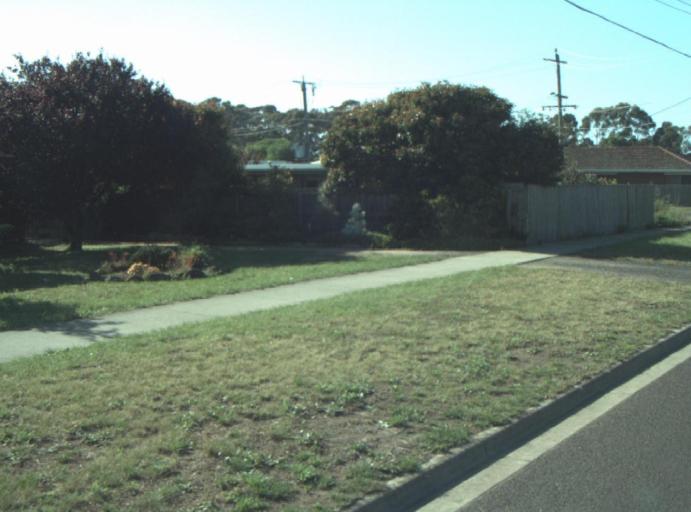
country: AU
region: Victoria
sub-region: Greater Geelong
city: Lara
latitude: -38.0220
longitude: 144.4066
